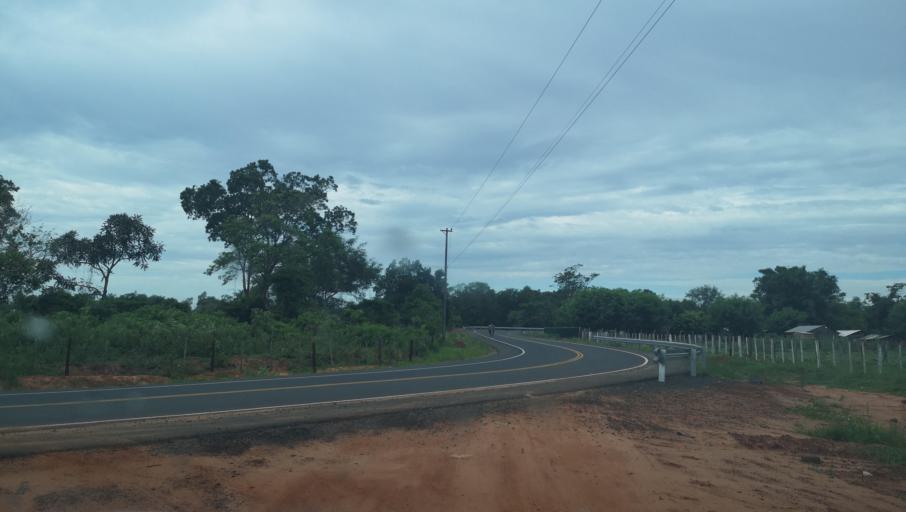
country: PY
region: San Pedro
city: Capiibary
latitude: -24.7427
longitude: -56.0363
